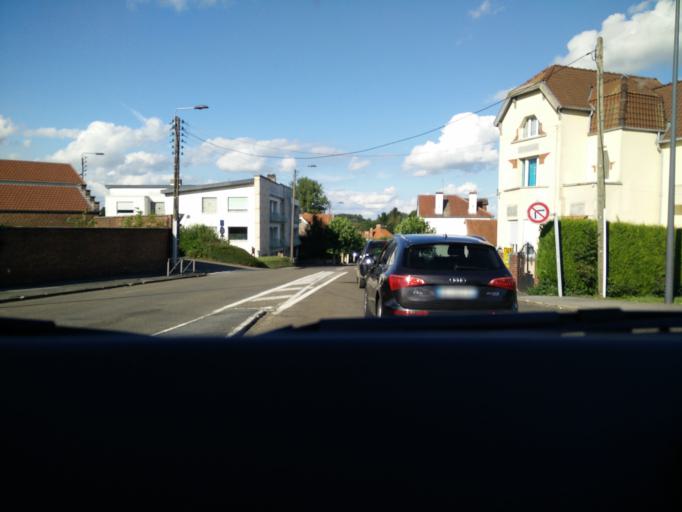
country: FR
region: Nord-Pas-de-Calais
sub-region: Departement du Nord
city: Maubeuge
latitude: 50.2829
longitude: 3.9760
